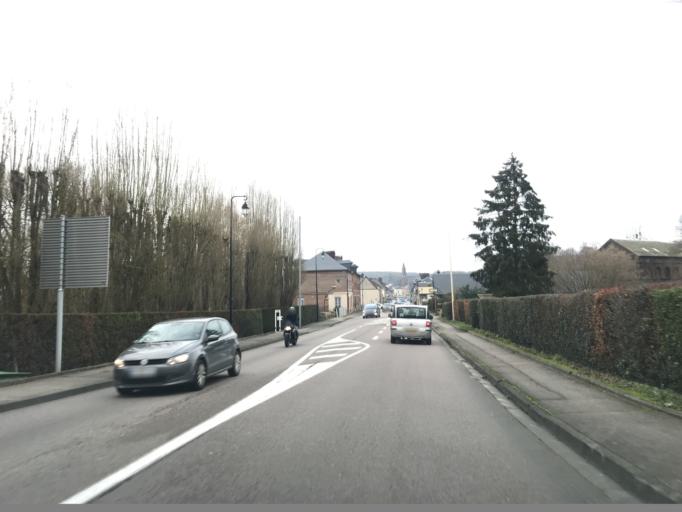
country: FR
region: Haute-Normandie
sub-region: Departement de l'Eure
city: Fleury-sur-Andelle
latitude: 49.3578
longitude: 1.3595
